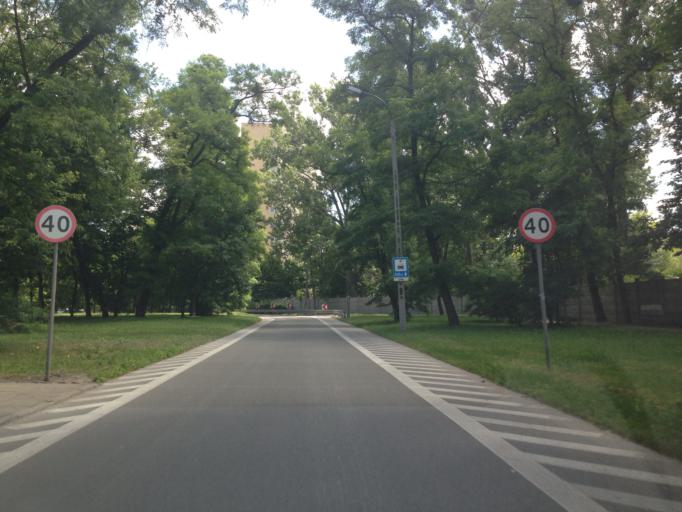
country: PL
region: Masovian Voivodeship
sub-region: Warszawa
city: Bemowo
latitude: 52.2550
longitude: 20.9061
